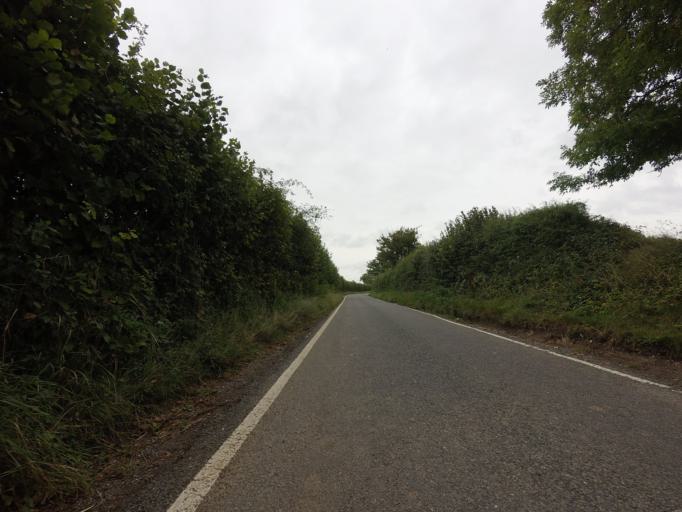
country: GB
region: England
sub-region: Hertfordshire
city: Reed
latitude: 51.9930
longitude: 0.0950
